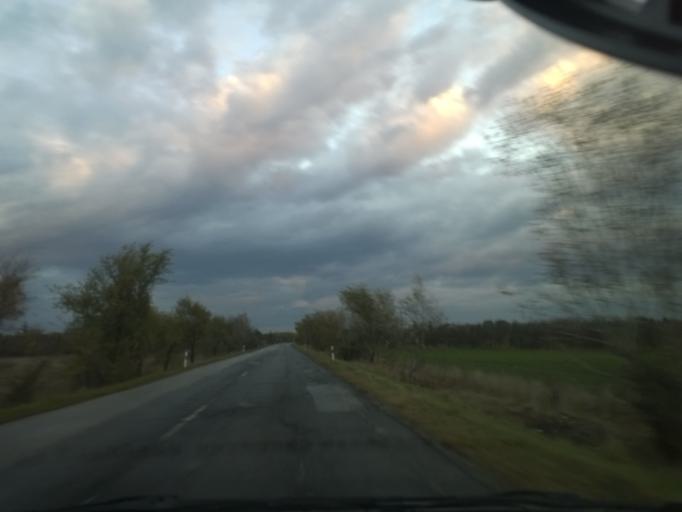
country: HU
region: Bacs-Kiskun
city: Tass
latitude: 47.0141
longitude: 19.0183
